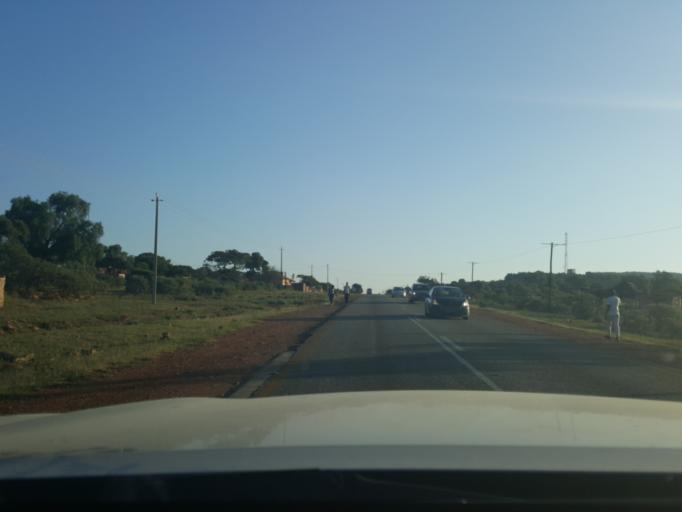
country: ZA
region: North-West
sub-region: Ngaka Modiri Molema District Municipality
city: Zeerust
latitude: -25.3311
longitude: 26.1172
